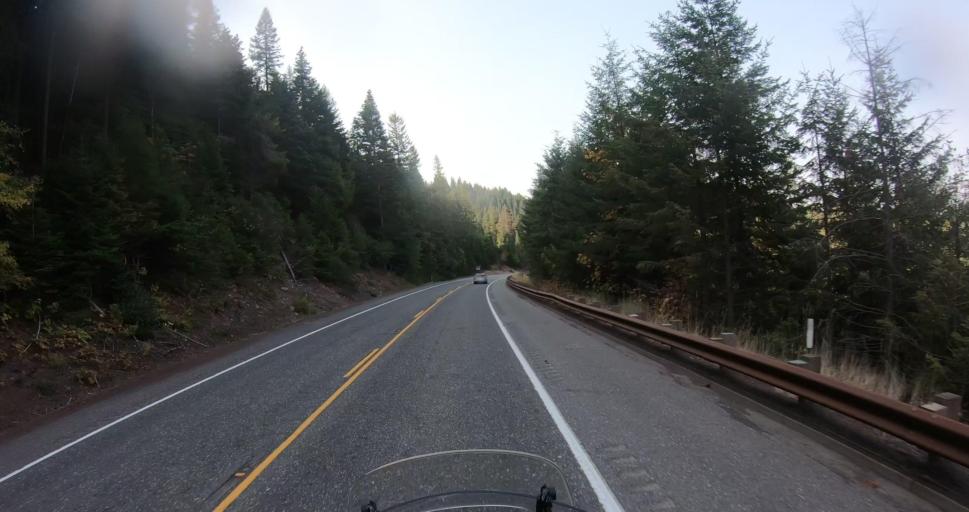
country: US
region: Oregon
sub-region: Hood River County
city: Odell
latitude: 45.4459
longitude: -121.5810
